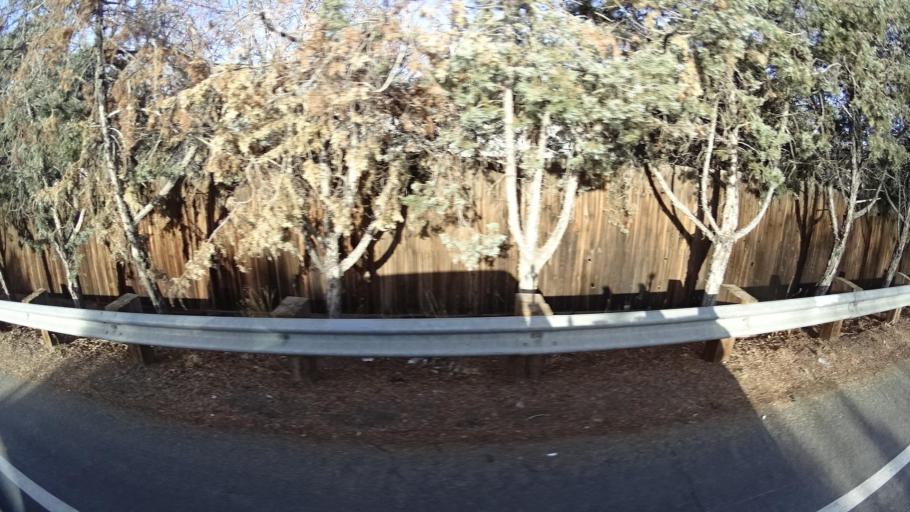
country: US
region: Nevada
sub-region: Washoe County
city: Sparks
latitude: 39.5562
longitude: -119.7792
